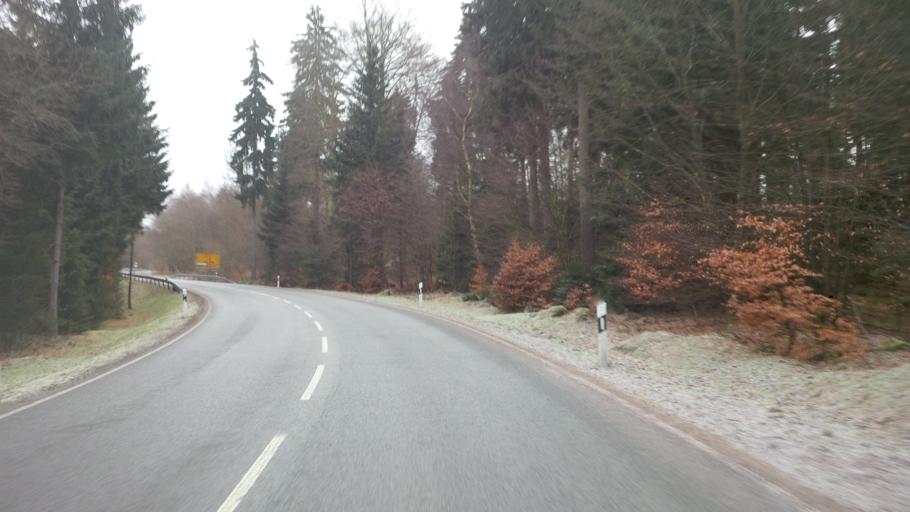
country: DE
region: Hesse
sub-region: Regierungsbezirk Darmstadt
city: Schmitten
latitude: 50.2468
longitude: 8.4860
